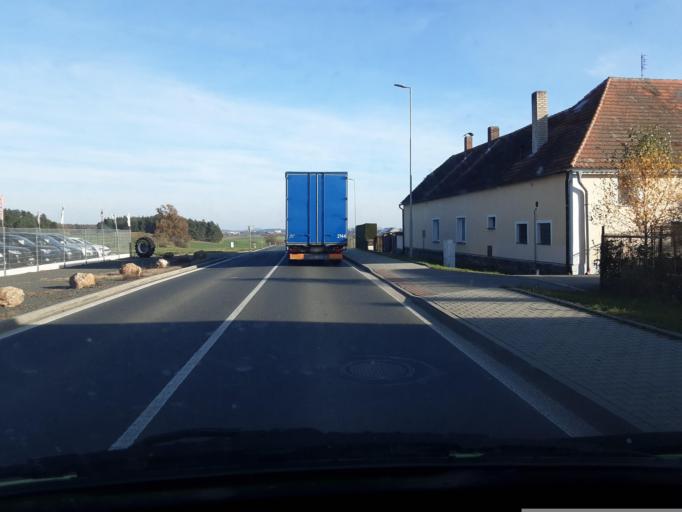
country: CZ
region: Plzensky
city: Horazd'ovice
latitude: 49.3306
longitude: 13.6559
